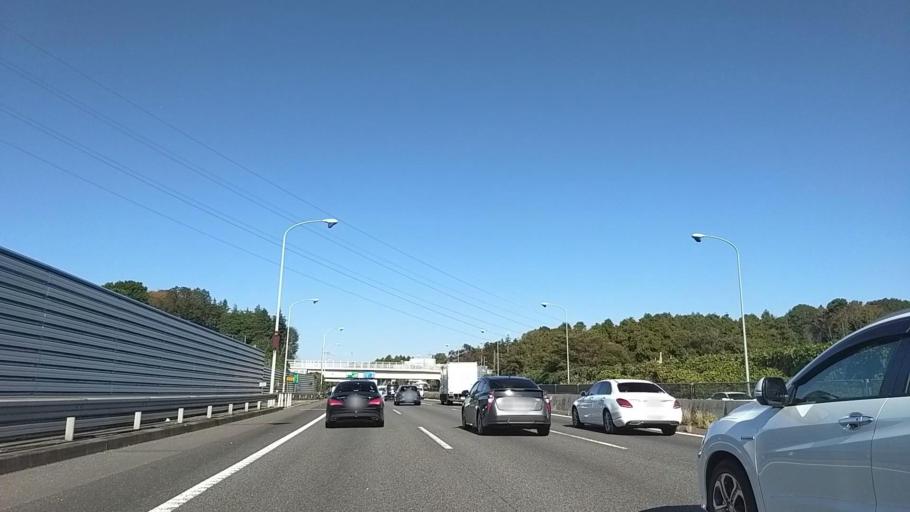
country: JP
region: Kanagawa
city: Minami-rinkan
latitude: 35.4886
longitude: 139.5068
